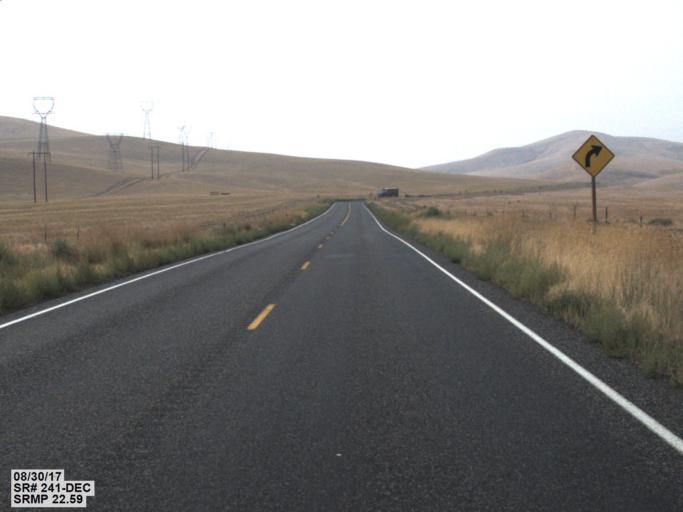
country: US
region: Washington
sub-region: Grant County
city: Desert Aire
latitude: 46.5022
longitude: -119.8892
